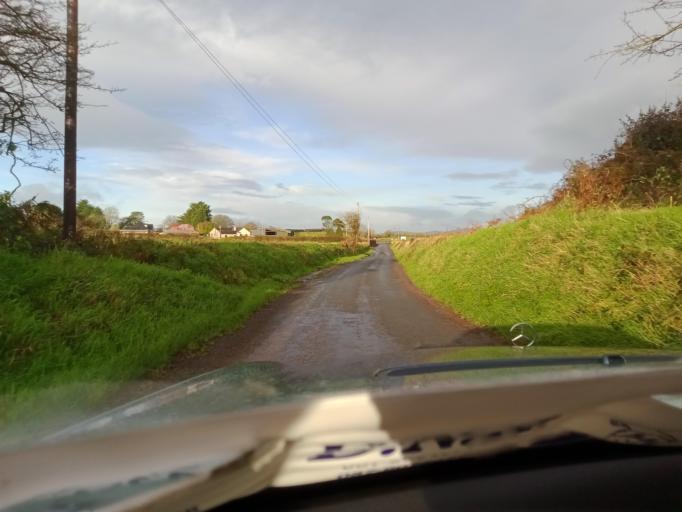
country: IE
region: Leinster
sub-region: Kilkenny
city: Mooncoin
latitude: 52.2806
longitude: -7.1974
